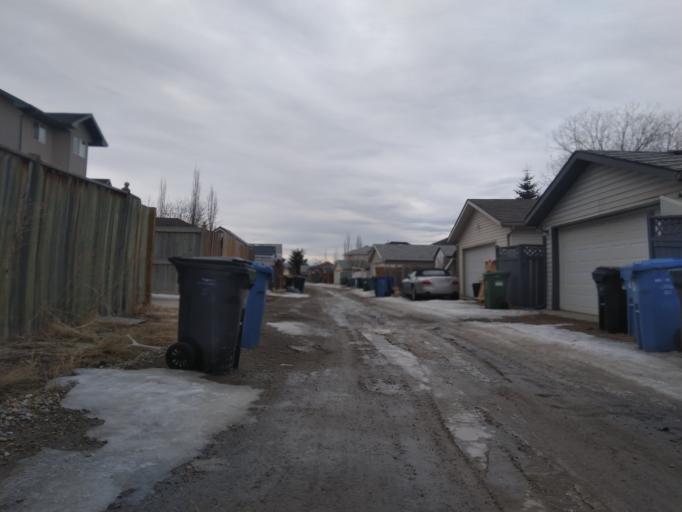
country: CA
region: Alberta
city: Calgary
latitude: 51.1675
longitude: -114.0438
